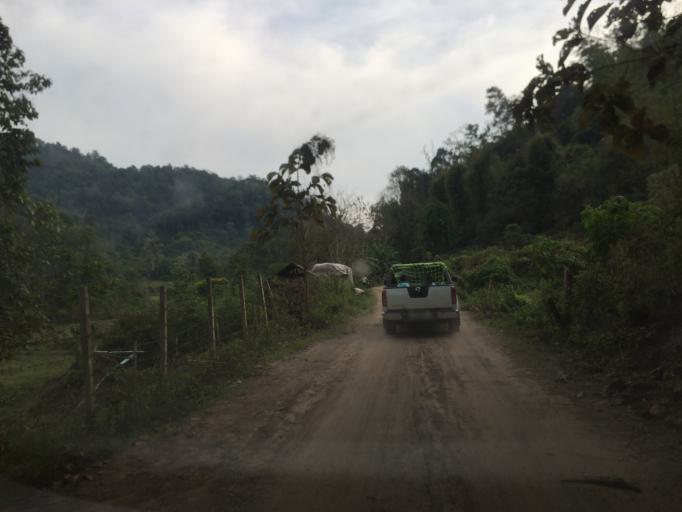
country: TH
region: Chiang Mai
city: Samoeng
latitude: 19.0075
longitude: 98.7299
